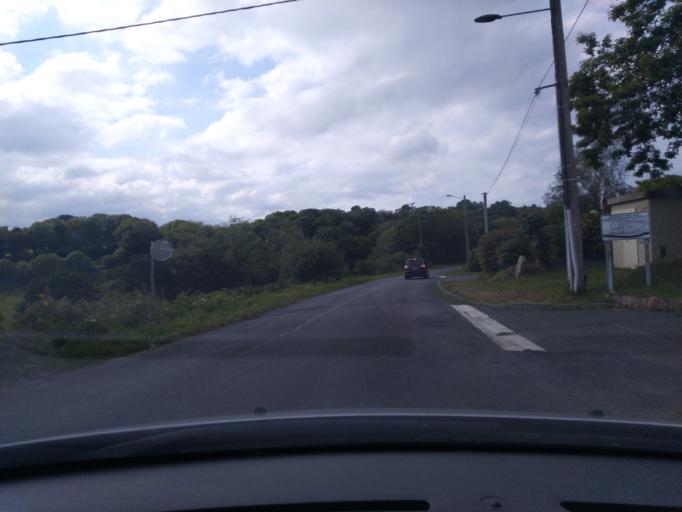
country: FR
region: Brittany
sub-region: Departement des Cotes-d'Armor
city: Saint-Quay-Perros
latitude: 48.7949
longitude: -3.4502
